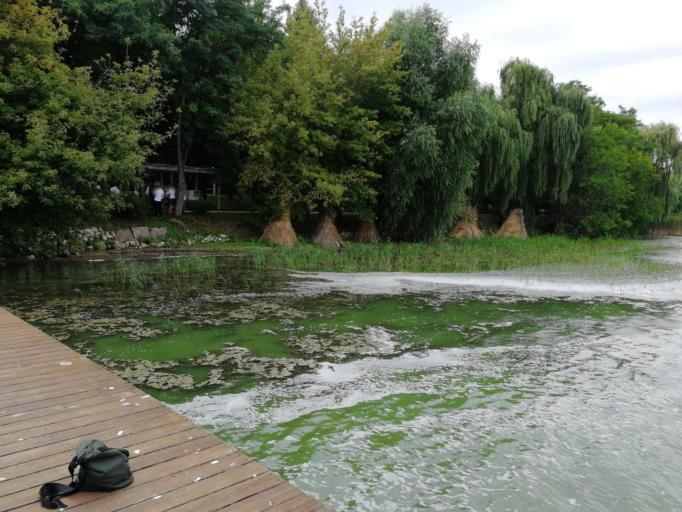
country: MD
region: Chisinau
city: Vatra
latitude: 47.1019
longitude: 28.7049
